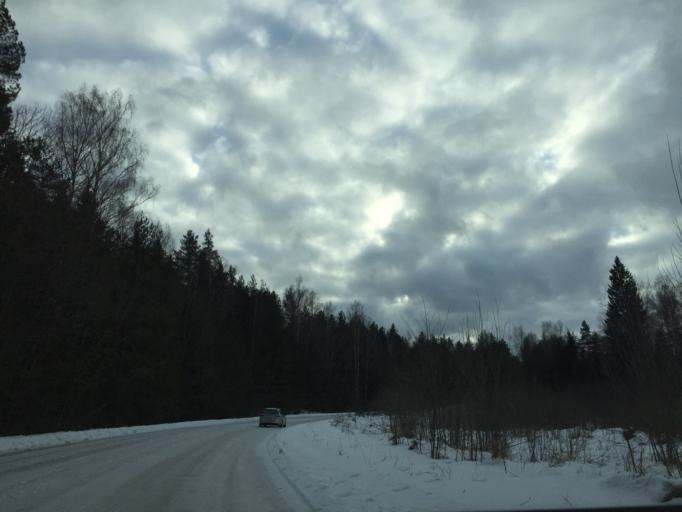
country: LV
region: Lielvarde
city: Lielvarde
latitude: 56.6230
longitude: 24.7744
